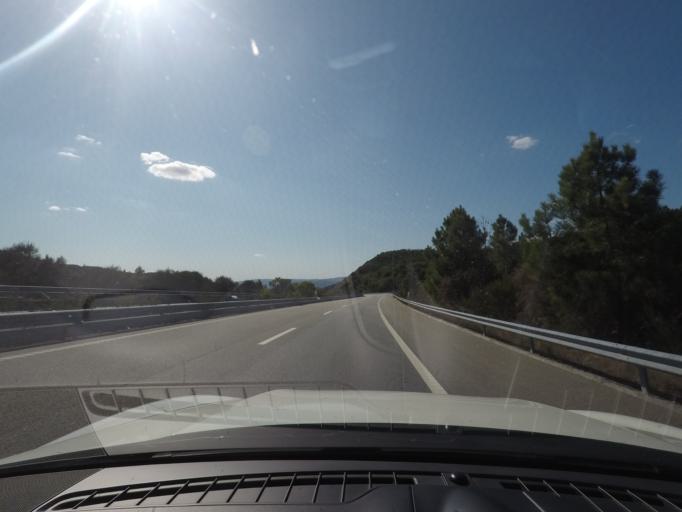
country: PT
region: Vila Real
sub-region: Ribeira de Pena
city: Ribeira de Pena
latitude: 41.4941
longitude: -7.8237
